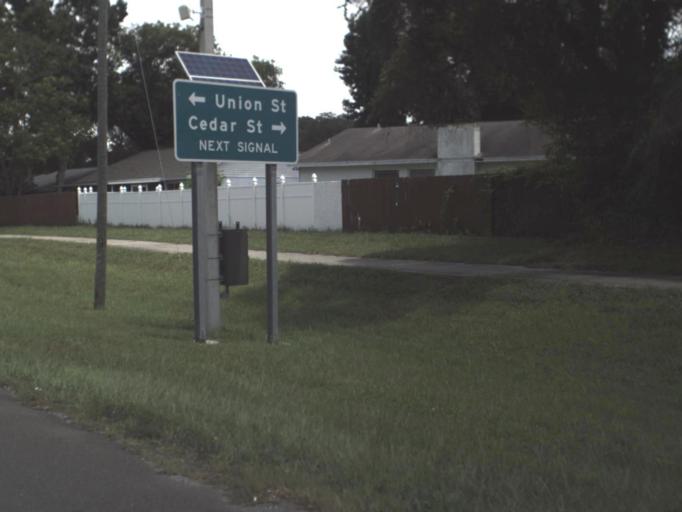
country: US
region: Florida
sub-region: Pinellas County
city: Safety Harbor
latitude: 27.9939
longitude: -82.7087
